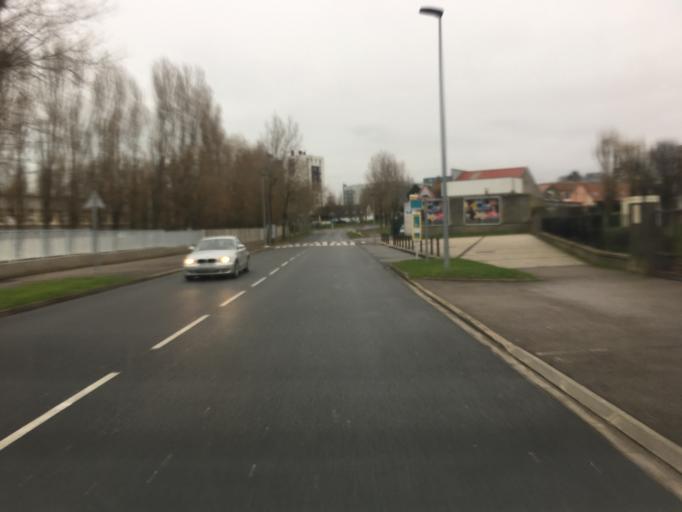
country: FR
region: Nord-Pas-de-Calais
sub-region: Departement du Pas-de-Calais
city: Le Portel
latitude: 50.7050
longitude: 1.5799
